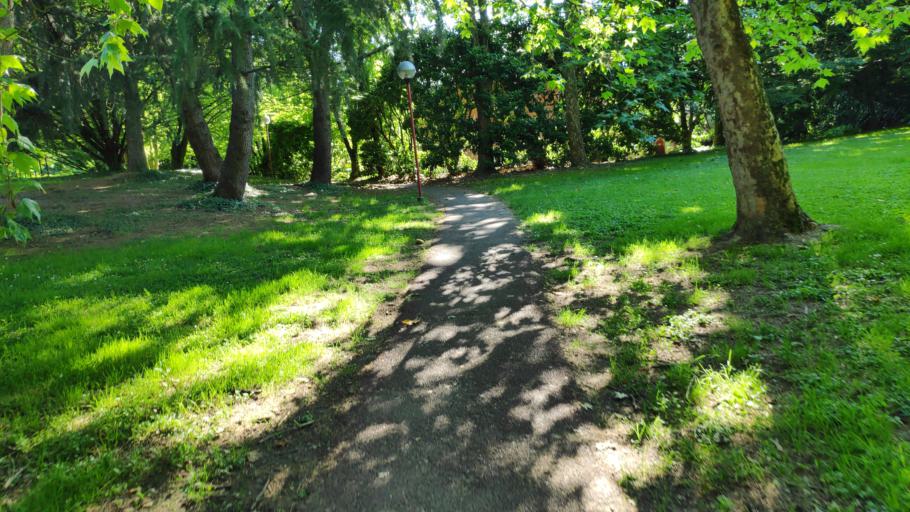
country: IT
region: Lombardy
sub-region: Citta metropolitana di Milano
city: Basiglio
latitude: 45.3565
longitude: 9.1594
